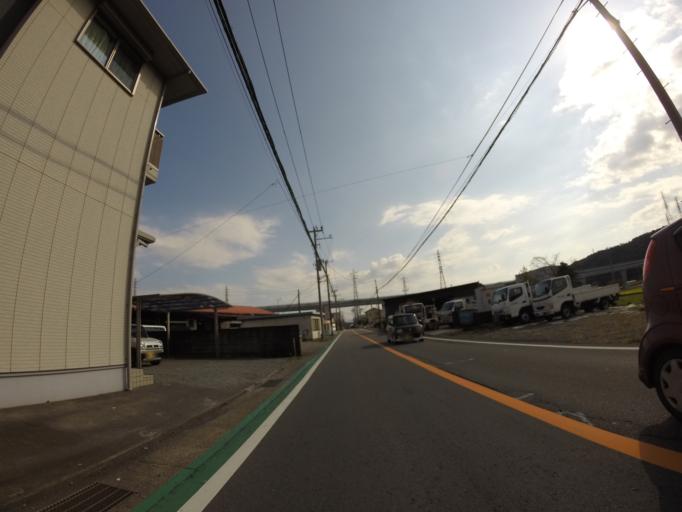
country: JP
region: Shizuoka
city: Fujinomiya
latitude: 35.1999
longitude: 138.6380
